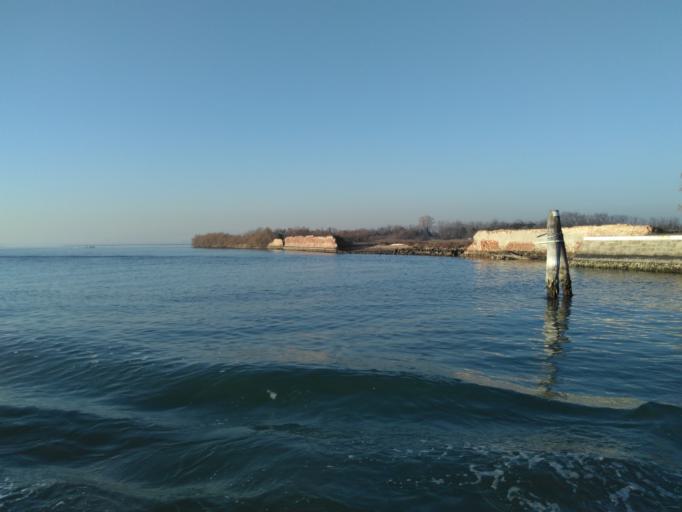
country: IT
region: Veneto
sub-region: Provincia di Venezia
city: Burano
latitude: 45.4858
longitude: 12.4026
